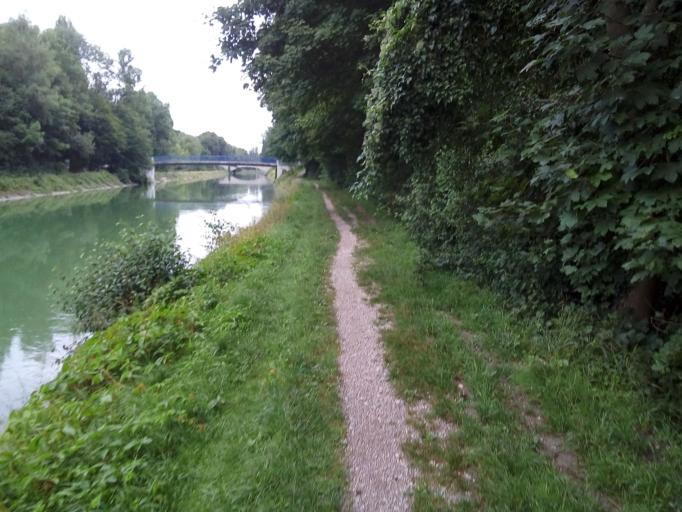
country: DE
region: Bavaria
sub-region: Upper Bavaria
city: Unterfoehring
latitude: 48.1750
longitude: 11.6257
